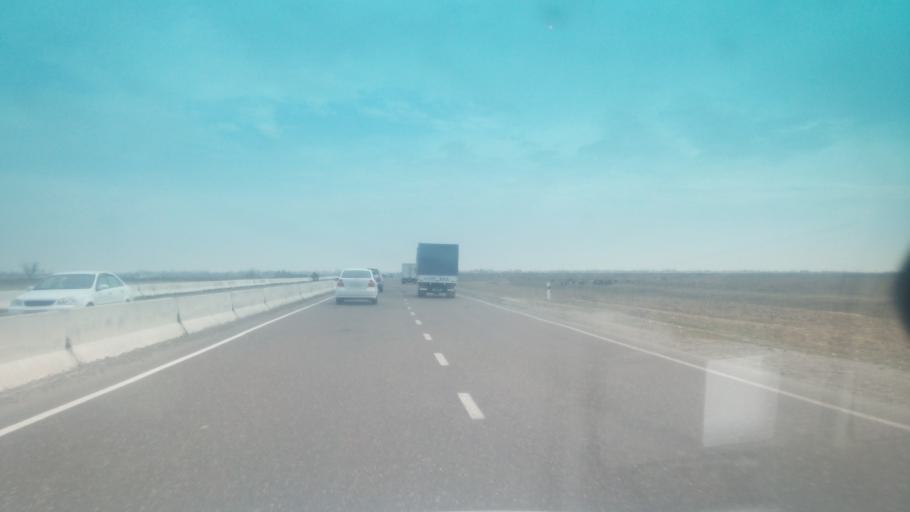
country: KZ
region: Ongtustik Qazaqstan
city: Myrzakent
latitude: 40.5129
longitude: 68.4909
